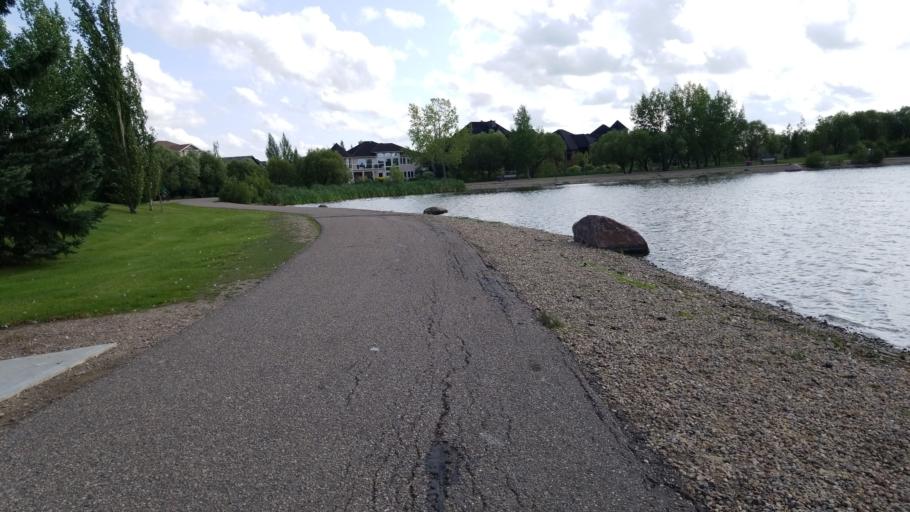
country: CA
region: Saskatchewan
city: Lloydminster
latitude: 53.2590
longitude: -110.0395
